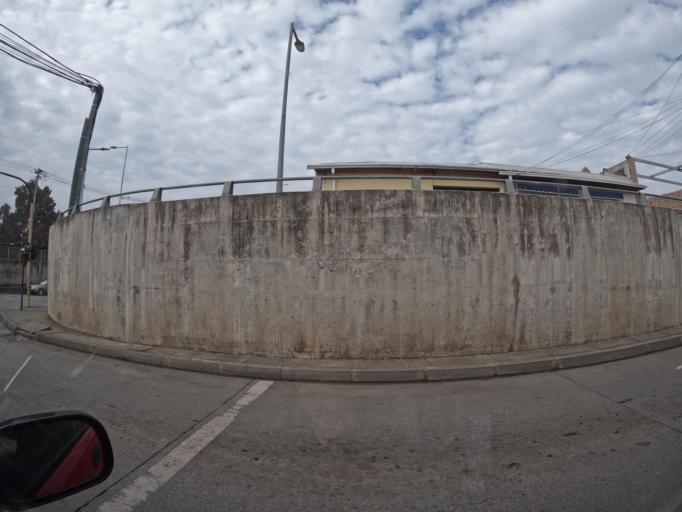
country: CL
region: Maule
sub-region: Provincia de Linares
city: Linares
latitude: -35.8416
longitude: -71.5891
